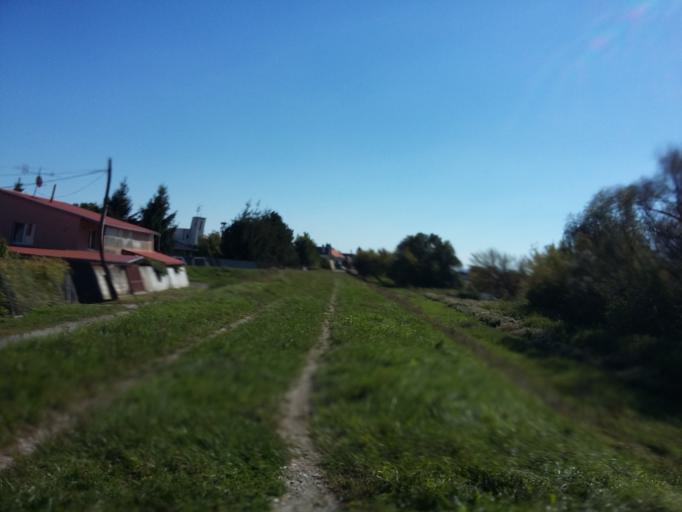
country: AT
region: Lower Austria
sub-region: Politischer Bezirk Ganserndorf
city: Marchegg
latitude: 48.3280
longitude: 16.9076
